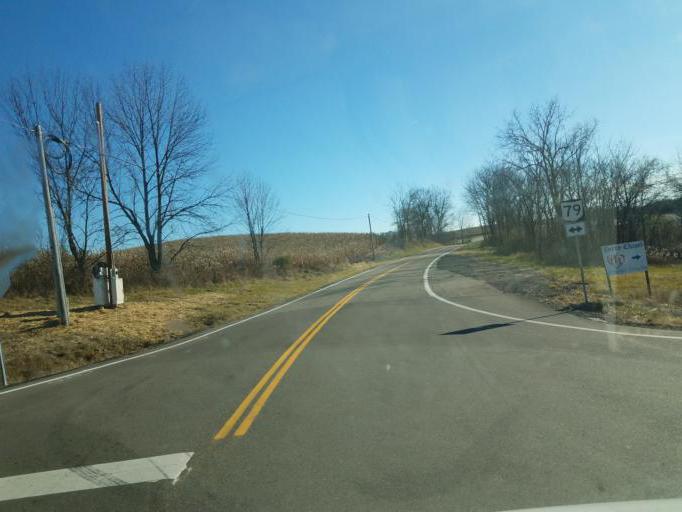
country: US
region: Ohio
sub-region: Muskingum County
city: Frazeysburg
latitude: 40.2727
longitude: -82.1164
